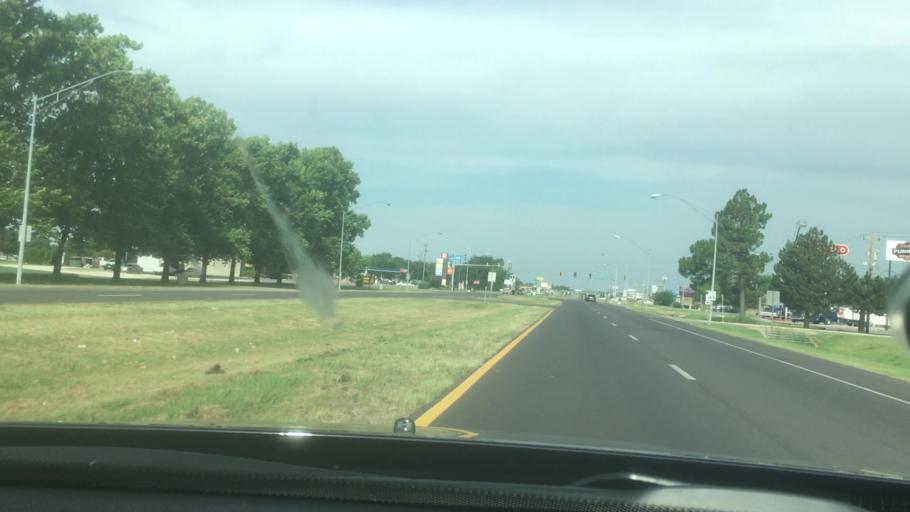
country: US
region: Oklahoma
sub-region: Garvin County
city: Pauls Valley
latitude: 34.7393
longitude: -97.2453
